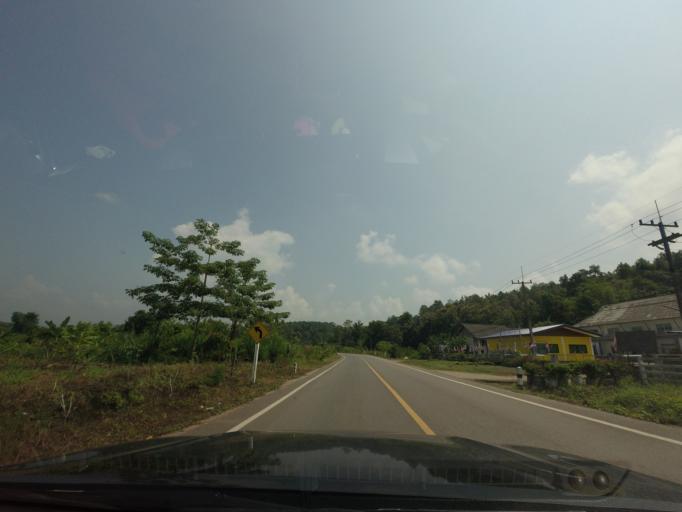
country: TH
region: Nan
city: Nan
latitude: 18.8640
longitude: 100.8286
